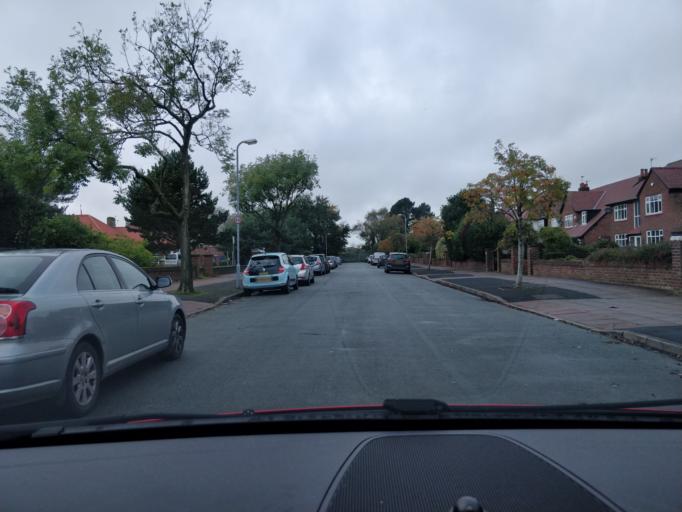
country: GB
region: England
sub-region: Sefton
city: Southport
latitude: 53.6127
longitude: -3.0228
